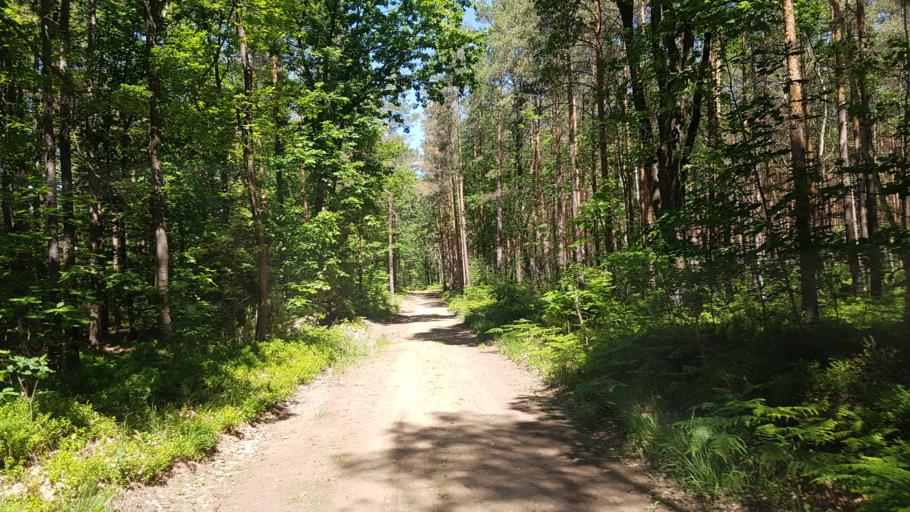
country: DE
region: Brandenburg
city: Hohenleipisch
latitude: 51.5337
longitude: 13.5770
